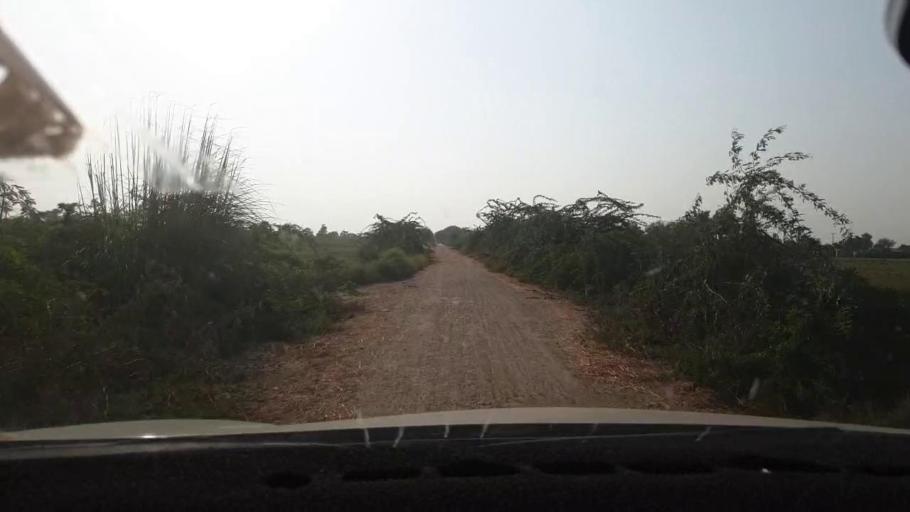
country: PK
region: Sindh
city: Berani
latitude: 25.7488
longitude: 68.7849
